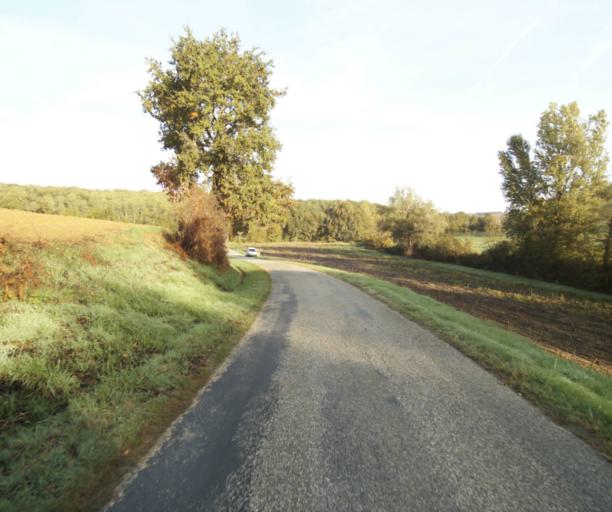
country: FR
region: Midi-Pyrenees
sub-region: Departement du Tarn-et-Garonne
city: Nohic
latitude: 43.9246
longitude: 1.4822
